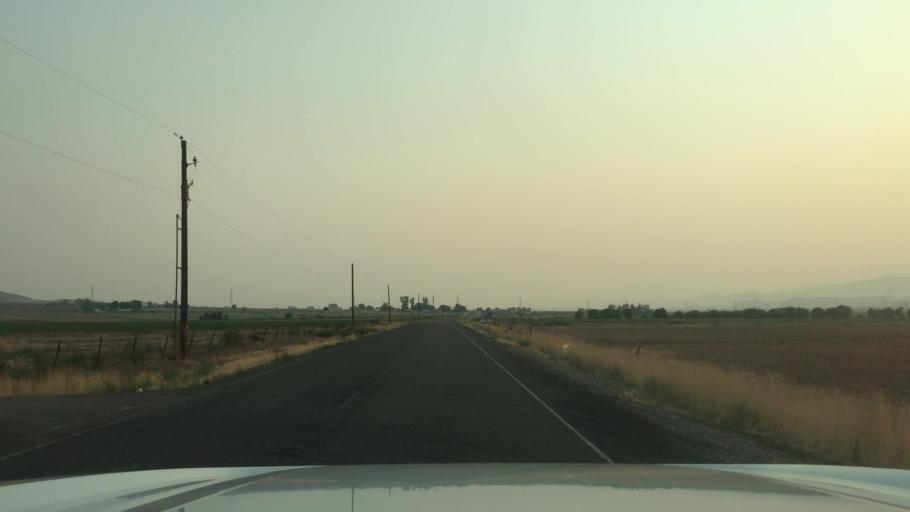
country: US
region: Utah
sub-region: Sevier County
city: Aurora
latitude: 38.8809
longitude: -111.9619
